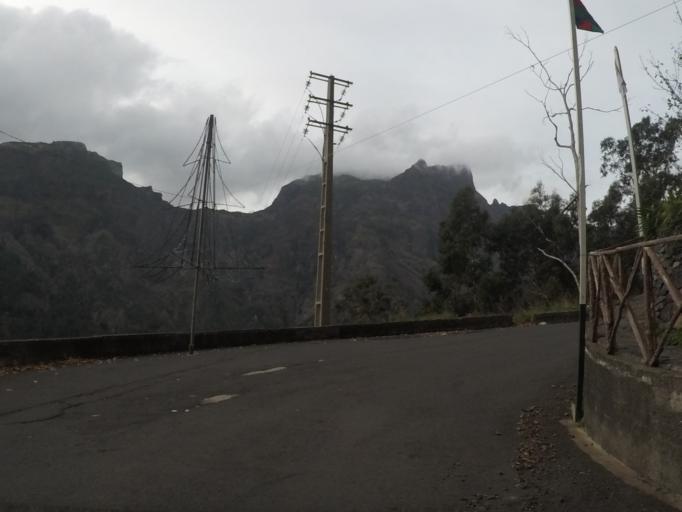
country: PT
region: Madeira
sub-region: Camara de Lobos
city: Curral das Freiras
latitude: 32.7251
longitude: -16.9626
